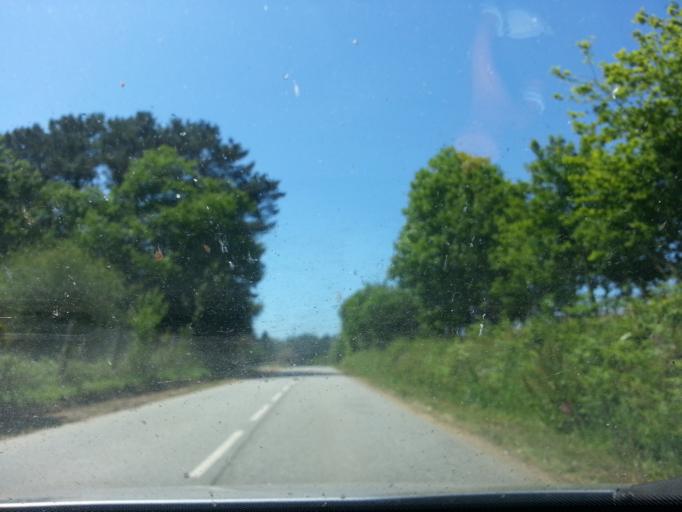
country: FR
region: Brittany
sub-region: Departement du Morbihan
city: Le Faouet
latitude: 48.0531
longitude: -3.4897
